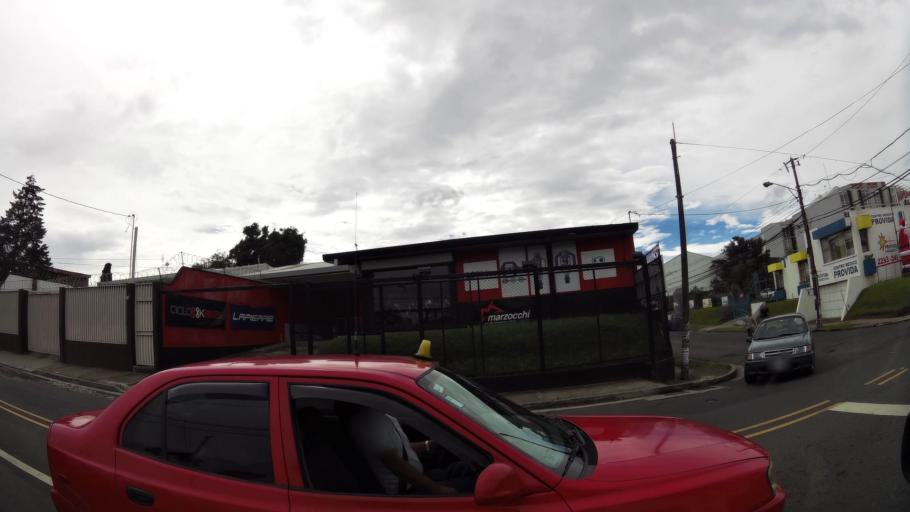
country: CR
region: San Jose
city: Sabanilla
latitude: 9.9432
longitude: -84.0413
